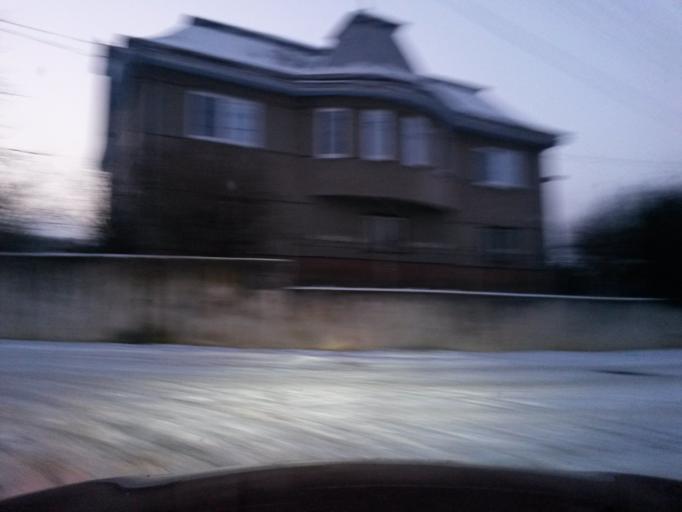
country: SK
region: Kosicky
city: Kosice
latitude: 48.7469
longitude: 21.3225
